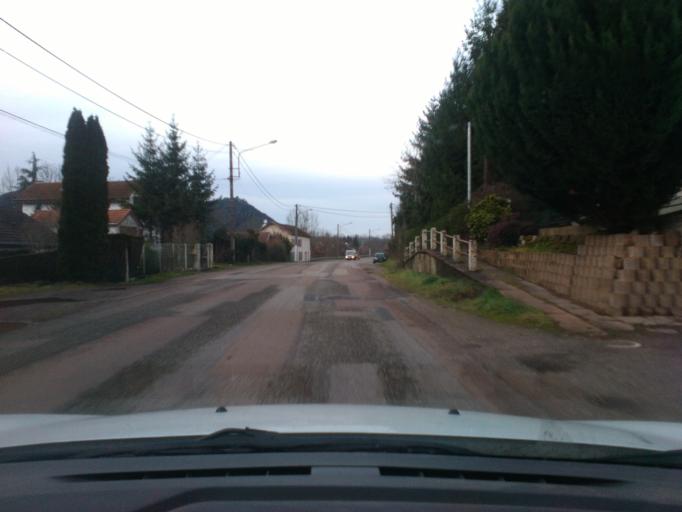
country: FR
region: Lorraine
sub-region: Departement des Vosges
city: Etival-Clairefontaine
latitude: 48.3591
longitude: 6.8785
